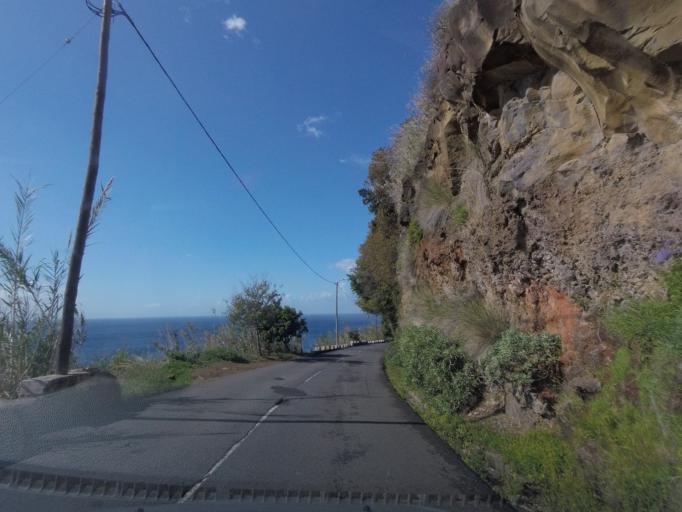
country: PT
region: Madeira
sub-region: Calheta
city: Estreito da Calheta
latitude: 32.7332
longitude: -17.2019
